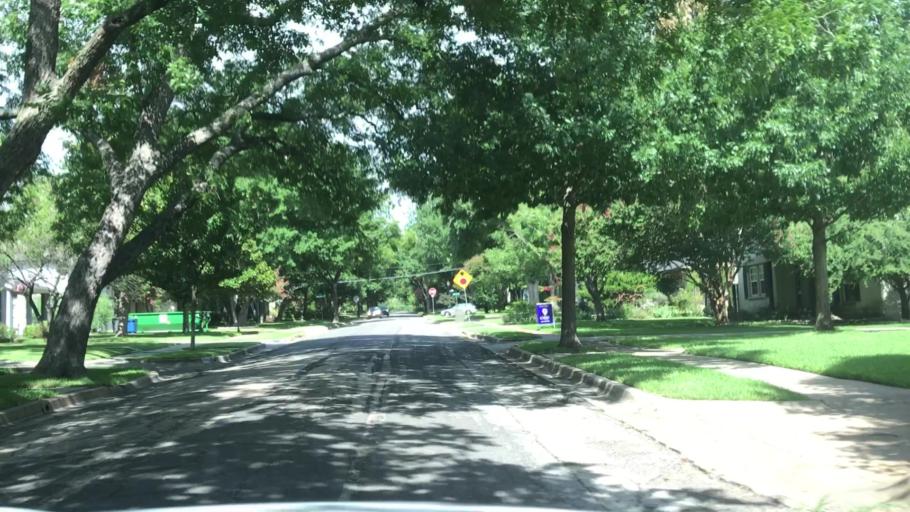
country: US
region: Texas
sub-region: Dallas County
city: Highland Park
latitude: 32.8299
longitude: -96.7786
